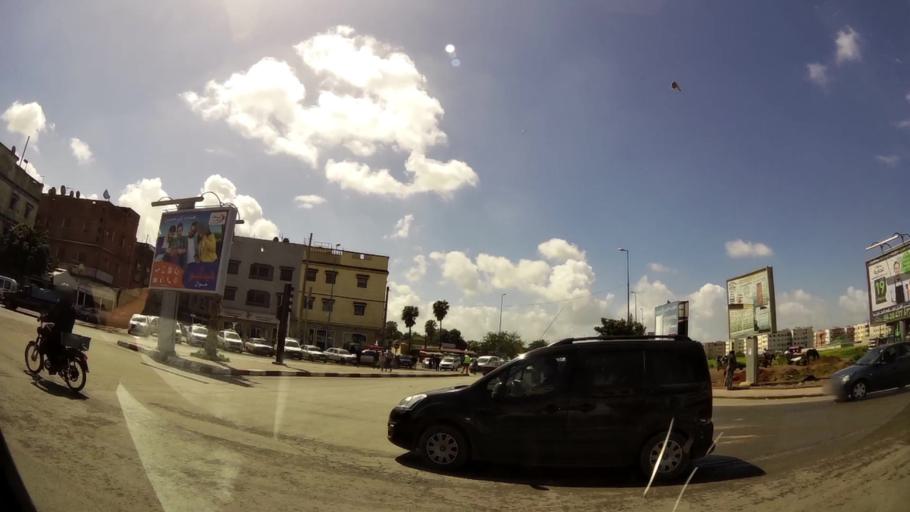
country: MA
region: Grand Casablanca
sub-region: Mediouna
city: Tit Mellil
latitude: 33.6350
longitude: -7.4513
